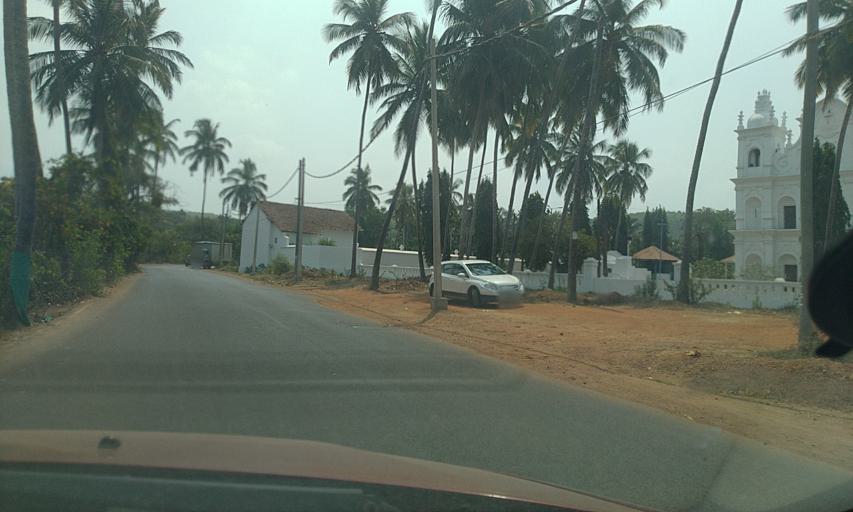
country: IN
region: Goa
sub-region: North Goa
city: Vagator
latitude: 15.5908
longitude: 73.7638
